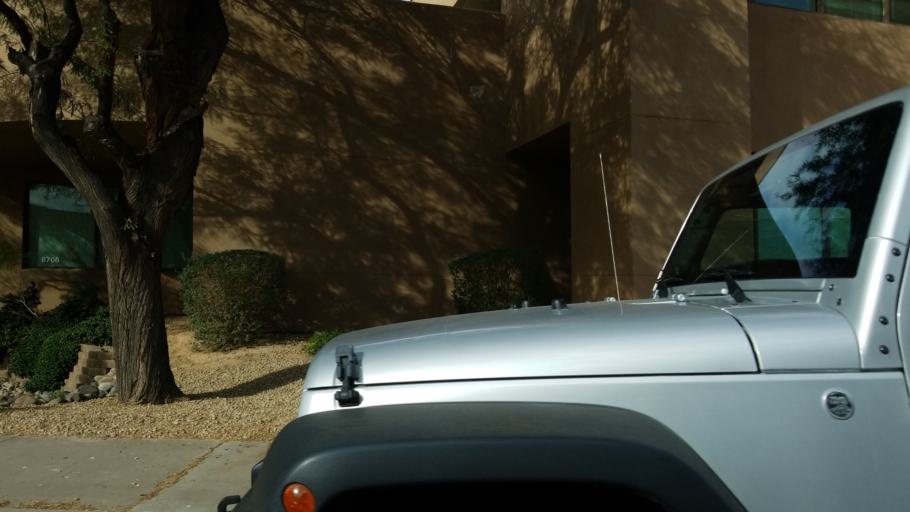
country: US
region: Arizona
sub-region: Maricopa County
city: Scottsdale
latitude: 33.5544
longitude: -111.8928
